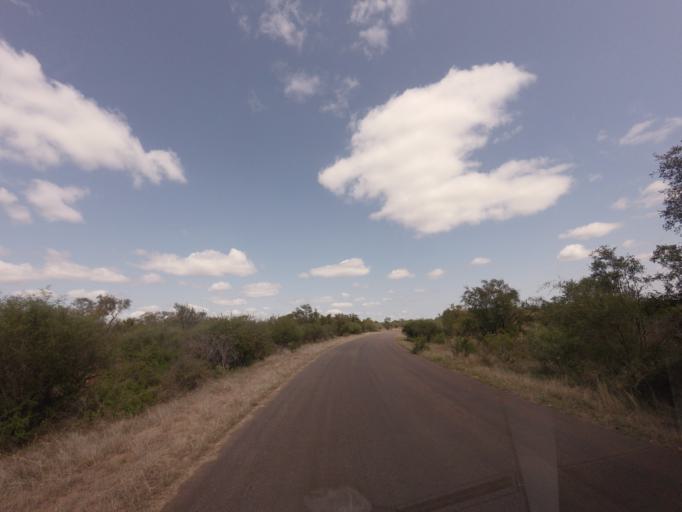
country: ZA
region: Mpumalanga
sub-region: Ehlanzeni District
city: Komatipoort
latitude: -25.1084
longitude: 31.9265
